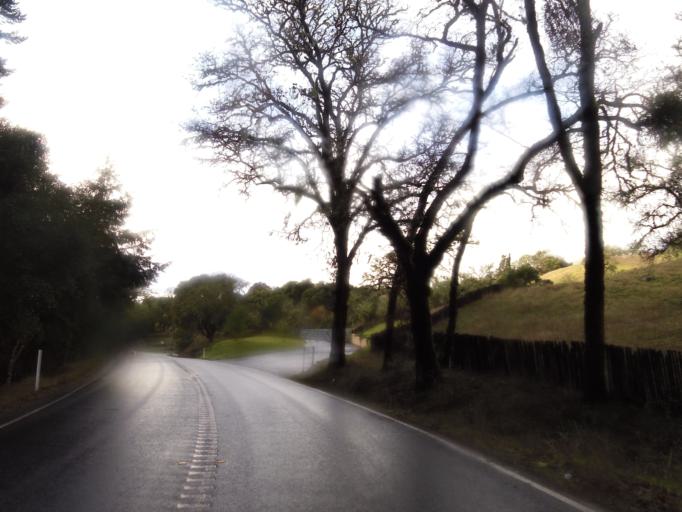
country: US
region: California
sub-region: Sonoma County
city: Cloverdale
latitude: 38.8871
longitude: -123.1235
